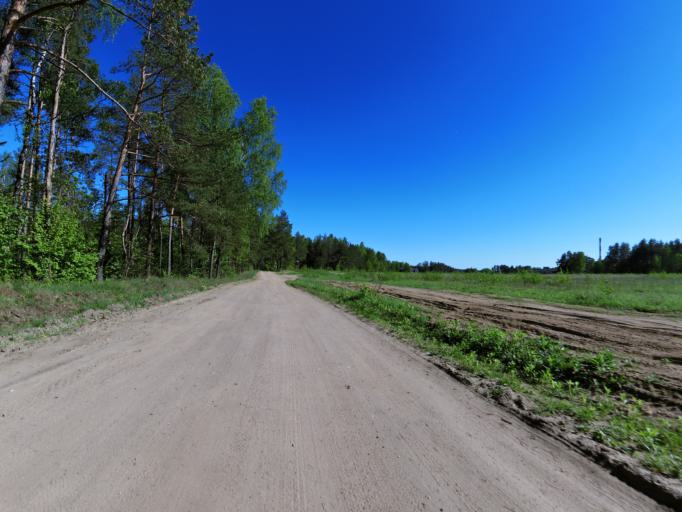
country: LT
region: Vilnius County
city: Pilaite
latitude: 54.6902
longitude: 25.1605
